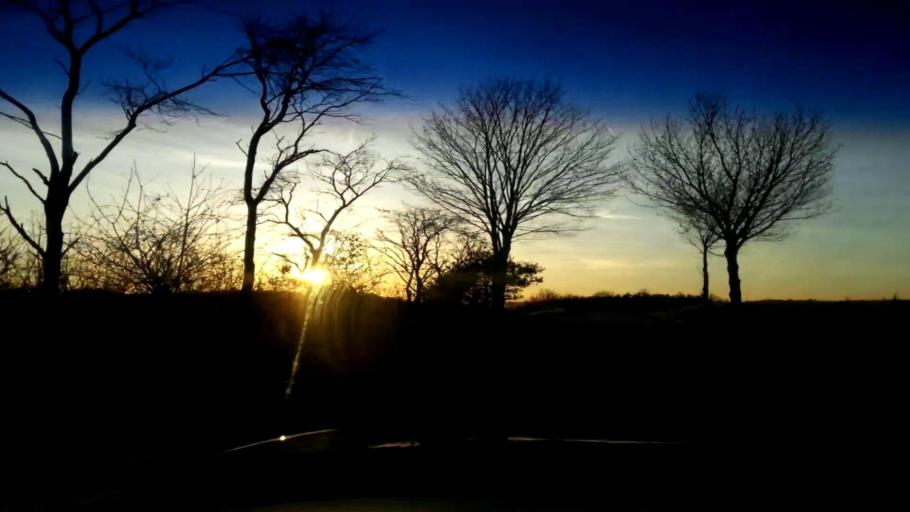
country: DE
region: Bavaria
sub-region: Upper Franconia
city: Zapfendorf
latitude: 50.0355
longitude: 10.9552
